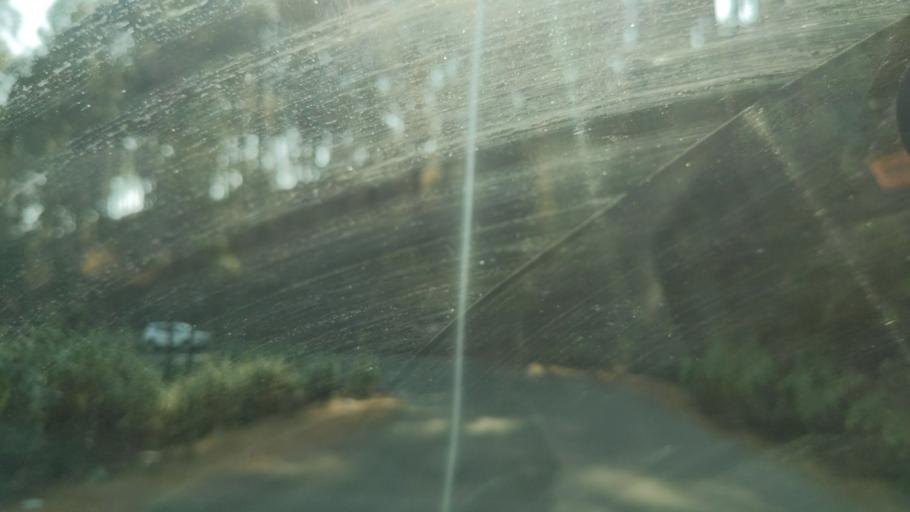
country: IN
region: Uttarakhand
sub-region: Naini Tal
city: Bhowali
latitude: 29.3909
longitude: 79.5397
